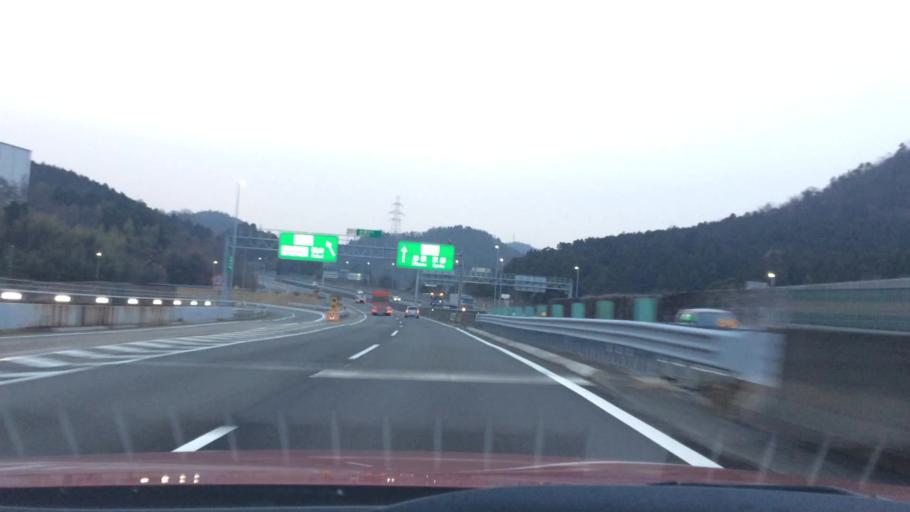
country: JP
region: Shiga Prefecture
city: Nagahama
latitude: 35.3174
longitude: 136.3217
